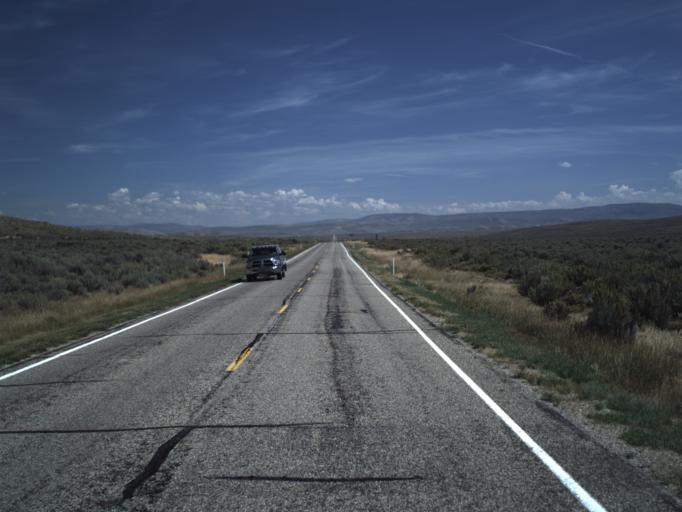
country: US
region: Utah
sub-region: Rich County
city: Randolph
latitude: 41.7693
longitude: -111.1564
